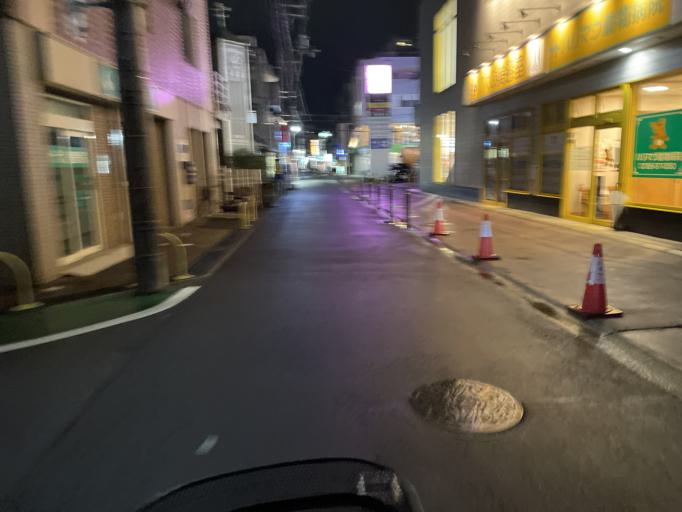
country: JP
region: Osaka
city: Ibaraki
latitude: 34.8153
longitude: 135.5792
